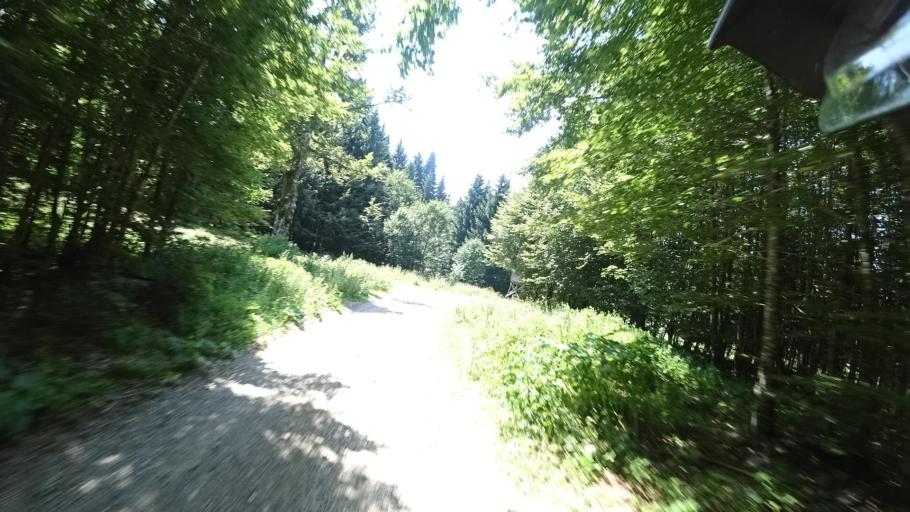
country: HR
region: Primorsko-Goranska
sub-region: Grad Delnice
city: Delnice
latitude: 45.2743
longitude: 14.9159
